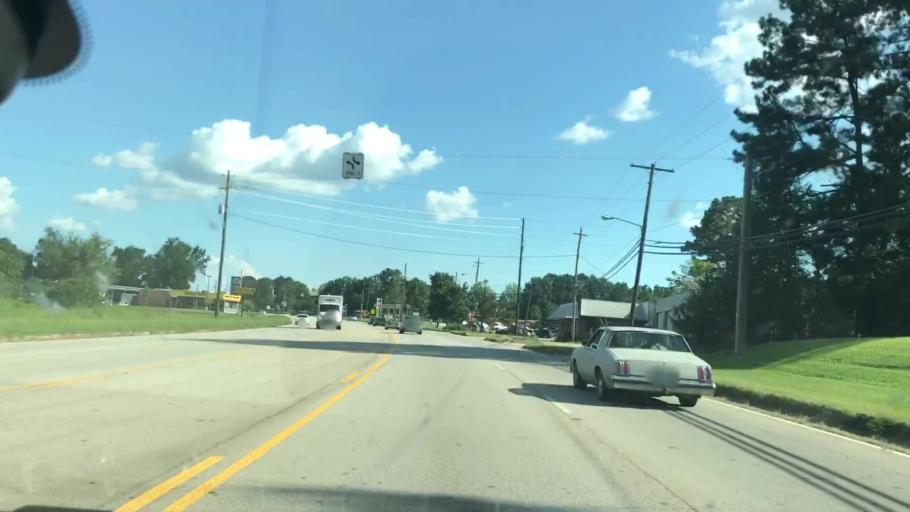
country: US
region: Georgia
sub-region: Troup County
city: La Grange
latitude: 33.0060
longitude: -85.0174
